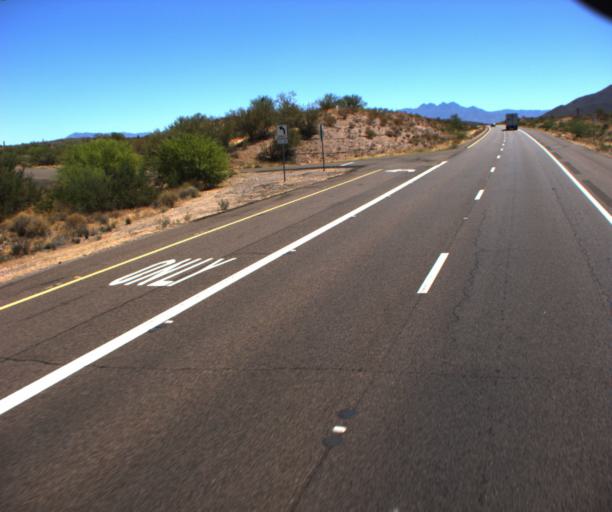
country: US
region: Arizona
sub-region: Maricopa County
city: Fountain Hills
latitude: 33.5819
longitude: -111.6163
